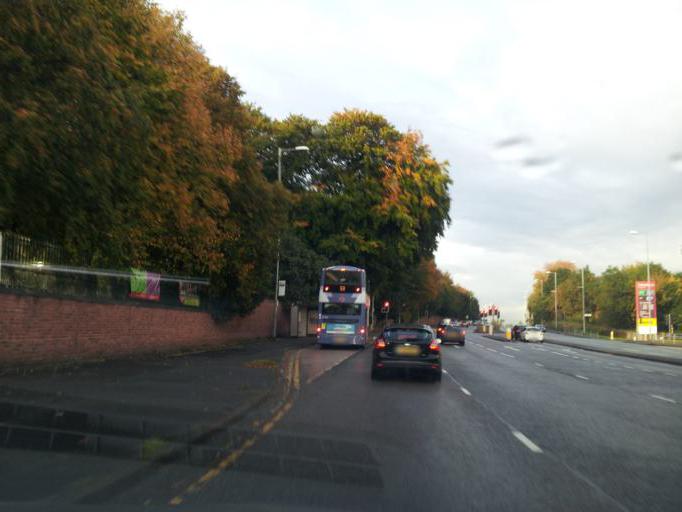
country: GB
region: England
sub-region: Manchester
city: Crumpsall
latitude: 53.5363
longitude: -2.2428
